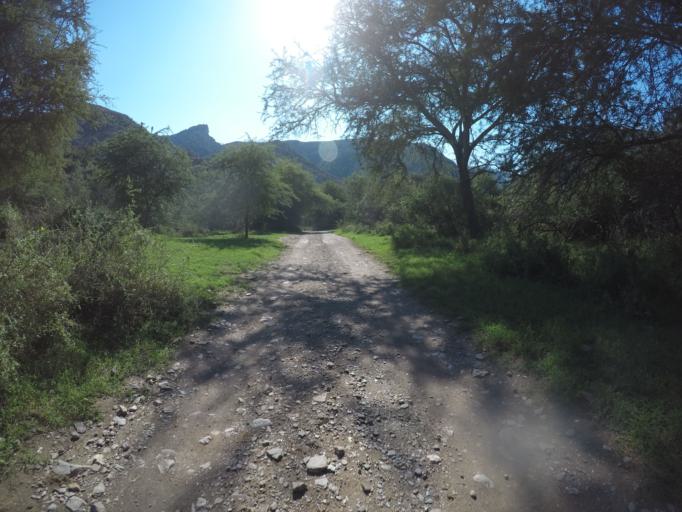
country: ZA
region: Eastern Cape
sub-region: Cacadu District Municipality
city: Kareedouw
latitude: -33.6557
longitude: 24.3656
